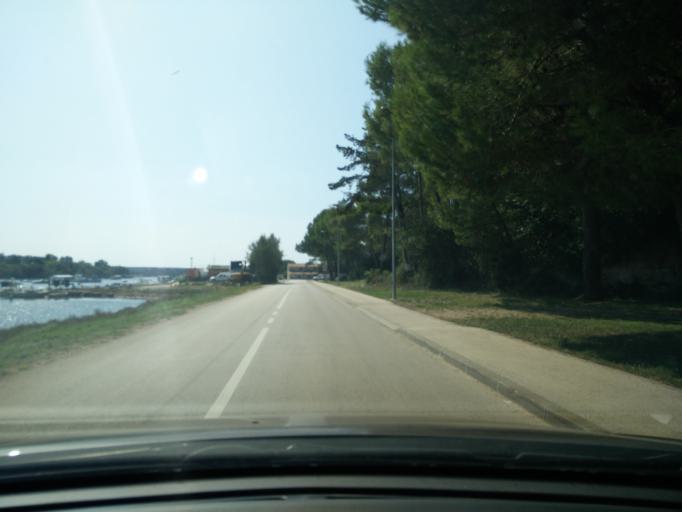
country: HR
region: Istarska
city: Novigrad
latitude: 45.2853
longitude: 13.5995
